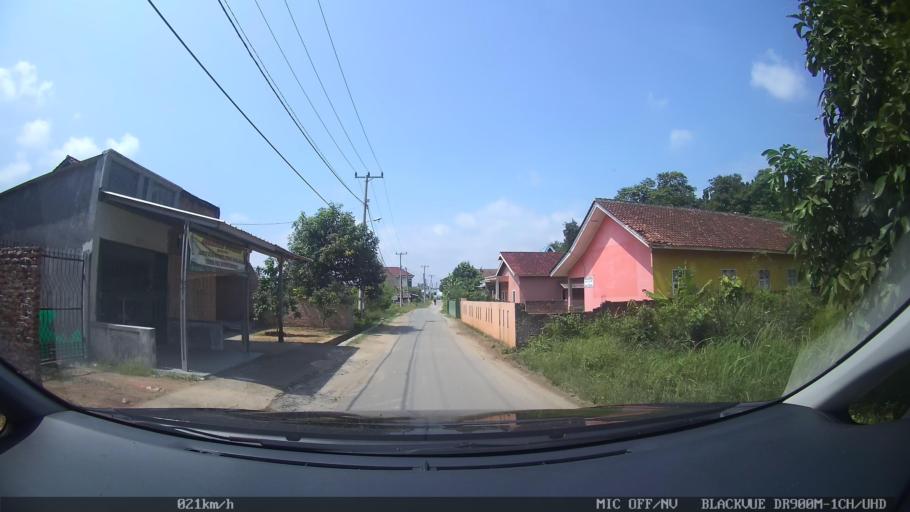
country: ID
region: Lampung
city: Kedaton
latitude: -5.3495
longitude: 105.2761
